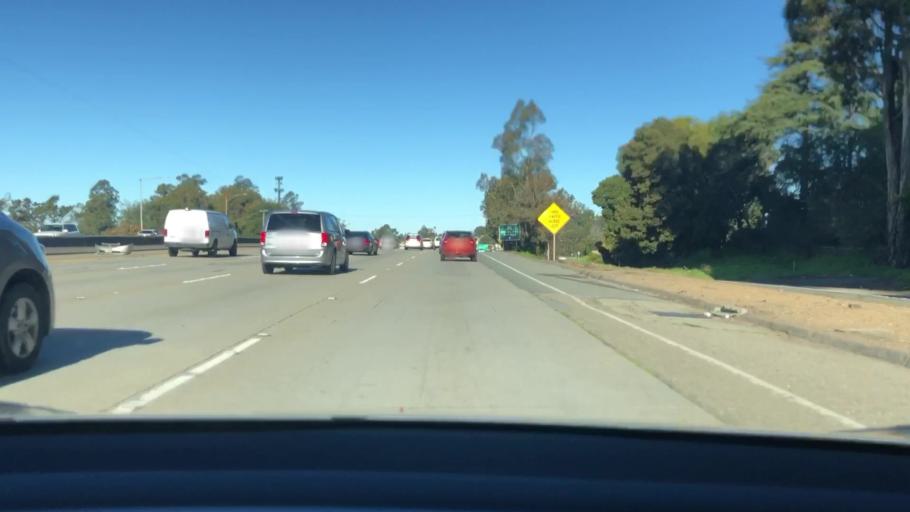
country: US
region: California
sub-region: Alameda County
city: San Leandro
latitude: 37.7802
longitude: -122.1716
